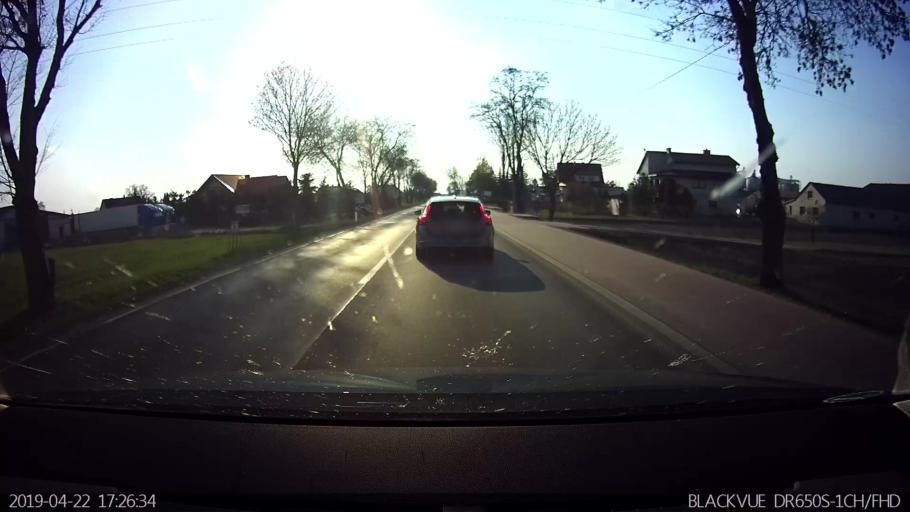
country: PL
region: Masovian Voivodeship
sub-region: Powiat sokolowski
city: Sokolow Podlaski
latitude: 52.3952
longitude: 22.2748
